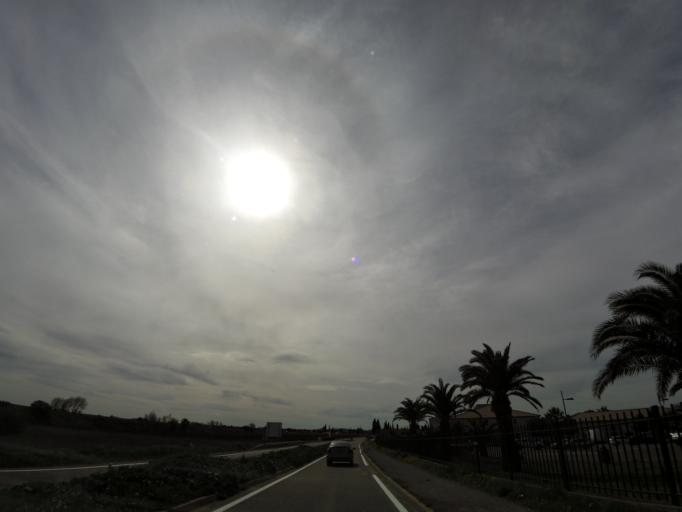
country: FR
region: Languedoc-Roussillon
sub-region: Departement du Gard
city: Gallargues-le-Montueux
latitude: 43.7164
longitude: 4.1811
